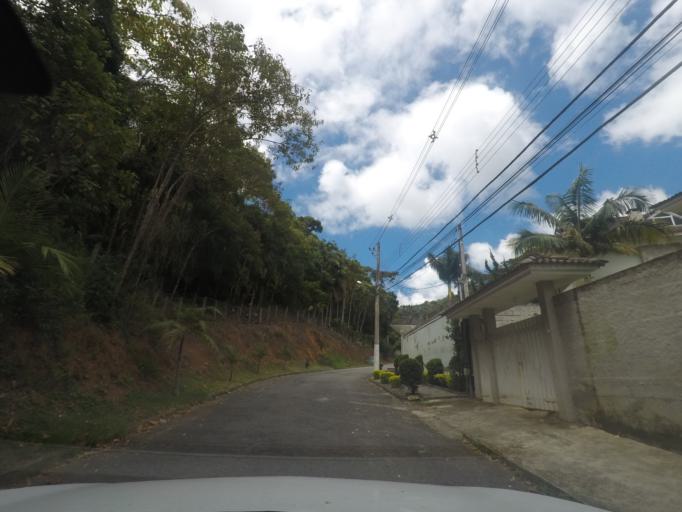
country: BR
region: Rio de Janeiro
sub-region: Teresopolis
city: Teresopolis
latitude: -22.4028
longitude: -42.9796
